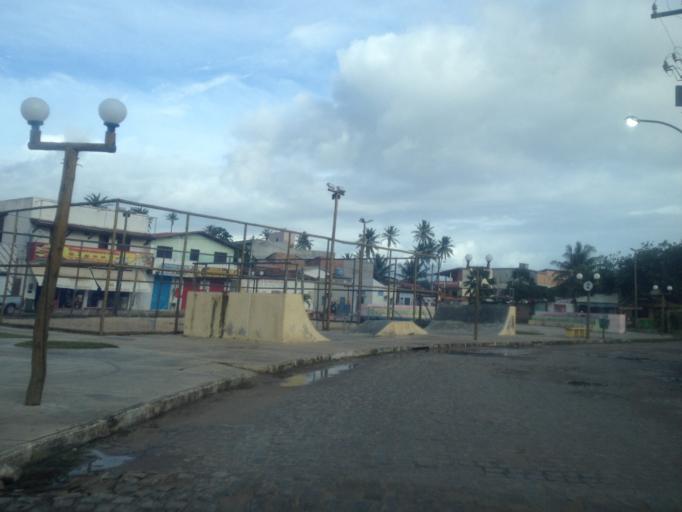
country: BR
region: Bahia
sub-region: Mata De Sao Joao
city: Mata de Sao Joao
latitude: -12.3901
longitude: -37.8823
